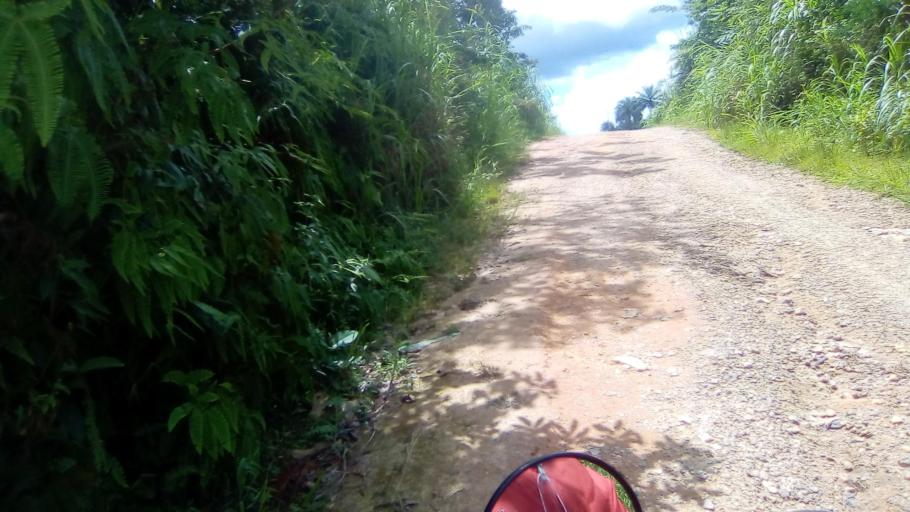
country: SL
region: Eastern Province
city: Simbakoro
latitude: 8.5409
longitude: -10.9403
